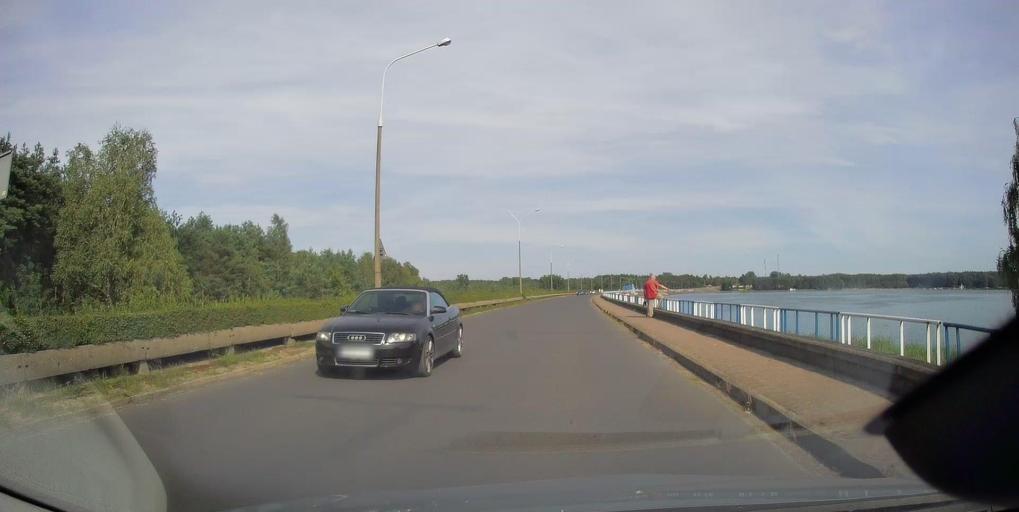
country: PL
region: Lodz Voivodeship
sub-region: Powiat tomaszowski
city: Tomaszow Mazowiecki
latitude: 51.4746
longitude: 19.9989
